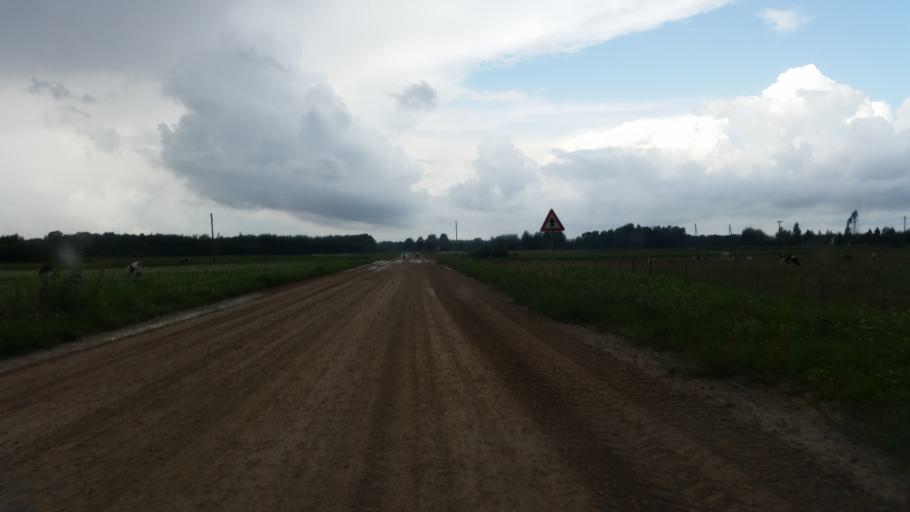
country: LV
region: Vecumnieki
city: Vecumnieki
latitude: 56.4280
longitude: 24.4632
